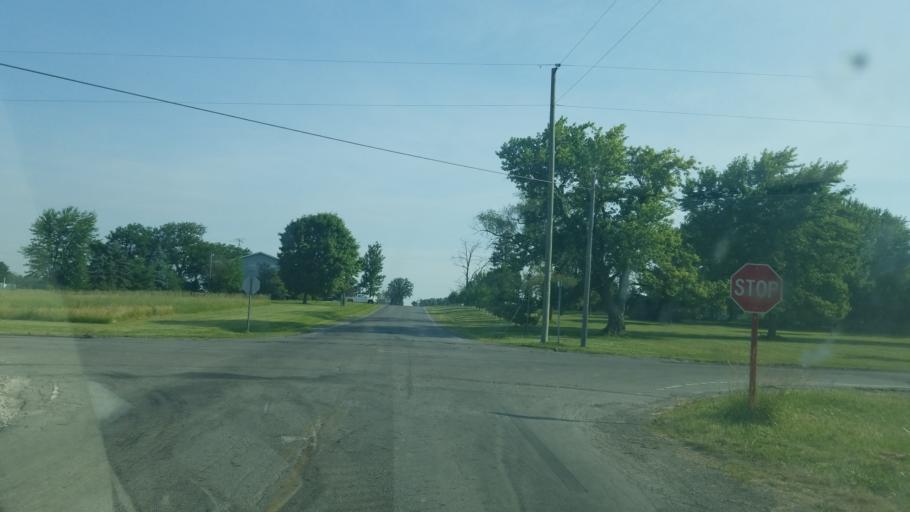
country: US
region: Ohio
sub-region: Hancock County
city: Arlington
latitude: 40.8923
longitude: -83.6986
